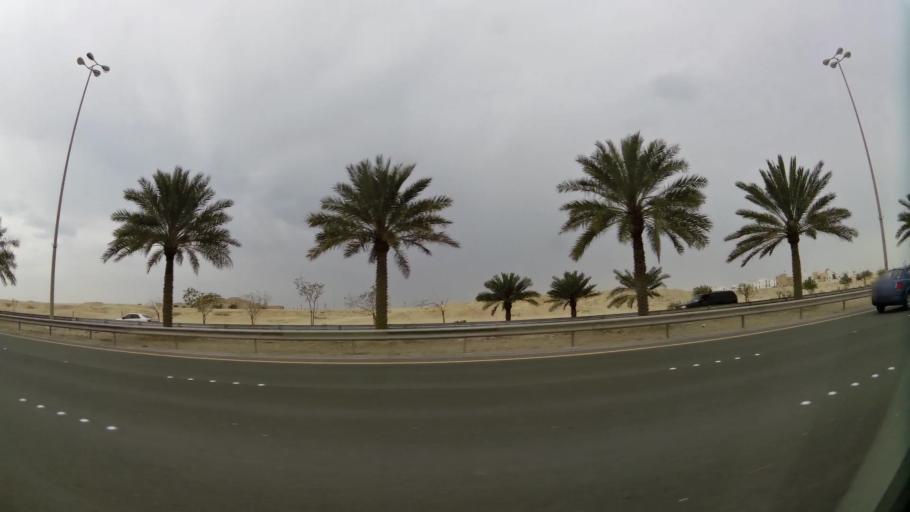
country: BH
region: Central Governorate
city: Dar Kulayb
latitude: 26.0868
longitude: 50.5155
